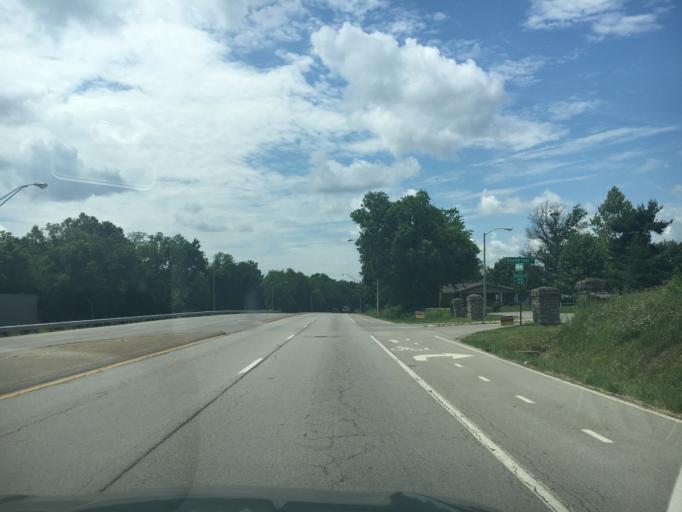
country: US
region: Kentucky
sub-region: Fayette County
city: Lexington-Fayette
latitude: 38.0719
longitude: -84.4628
